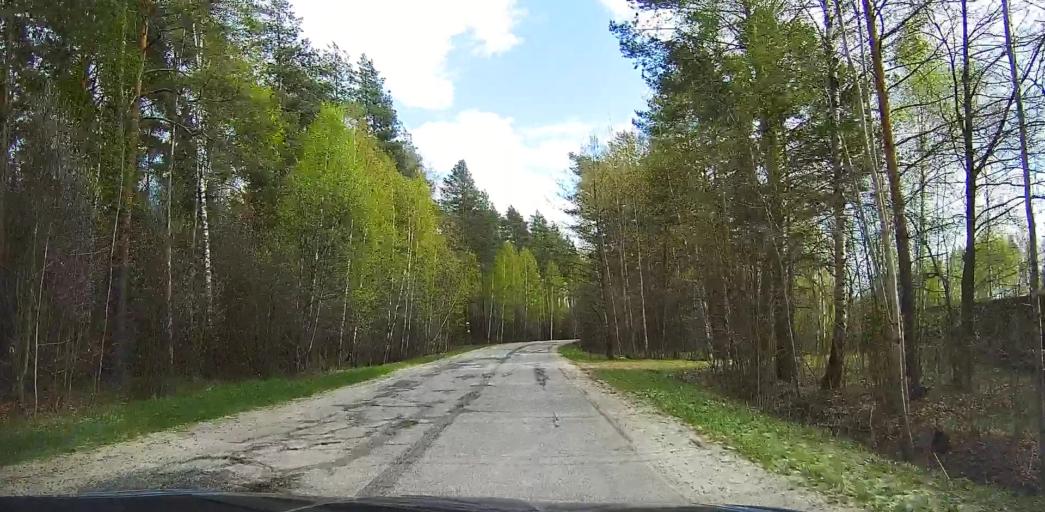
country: RU
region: Moskovskaya
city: Davydovo
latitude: 55.6446
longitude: 38.7726
